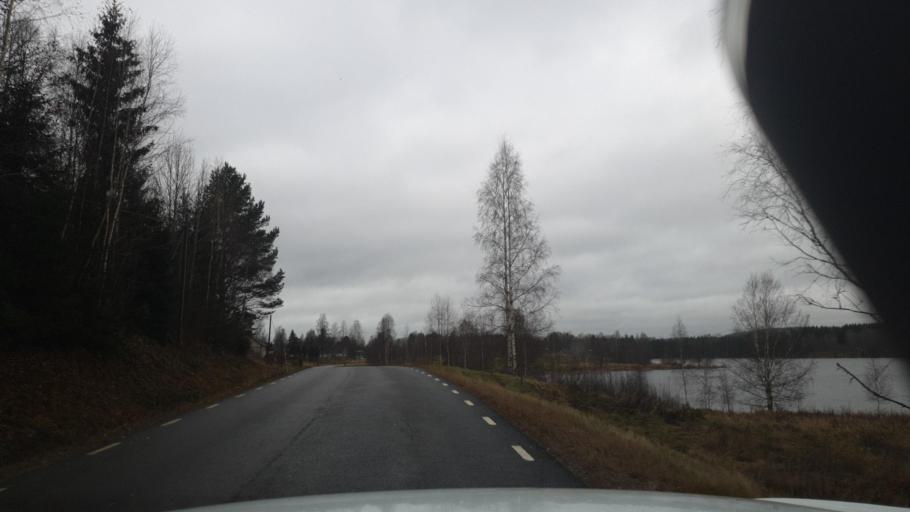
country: SE
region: Vaermland
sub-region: Eda Kommun
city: Charlottenberg
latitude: 59.9448
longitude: 12.5211
